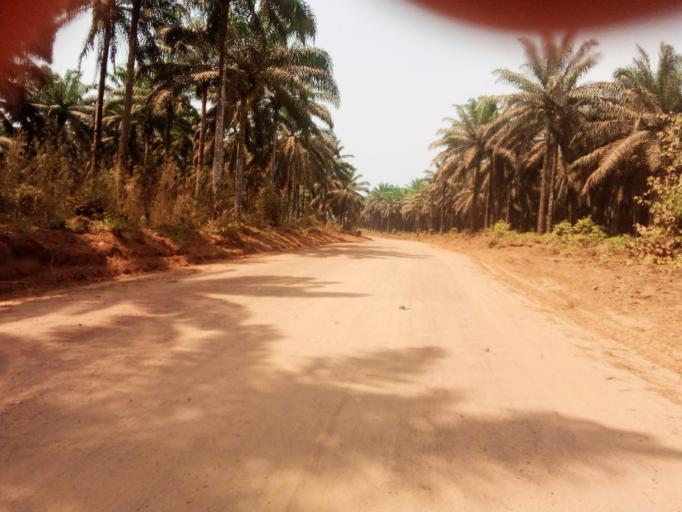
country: SL
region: Southern Province
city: Sumbuya
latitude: 7.6202
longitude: -12.1228
